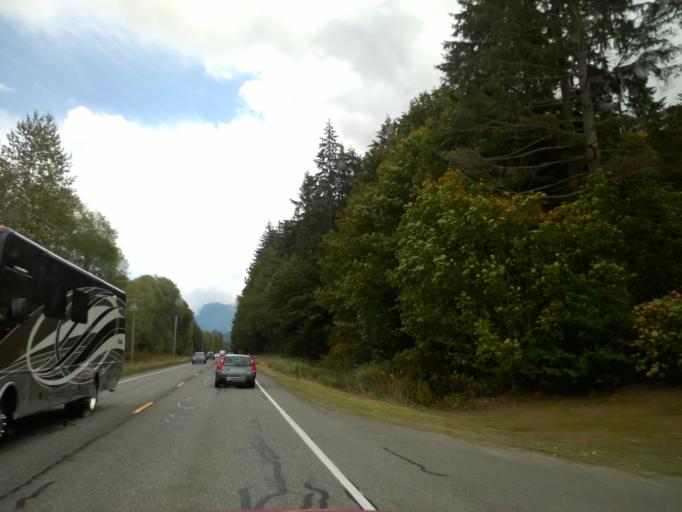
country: US
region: Washington
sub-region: Snohomish County
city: Gold Bar
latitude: 47.7655
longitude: -121.4768
